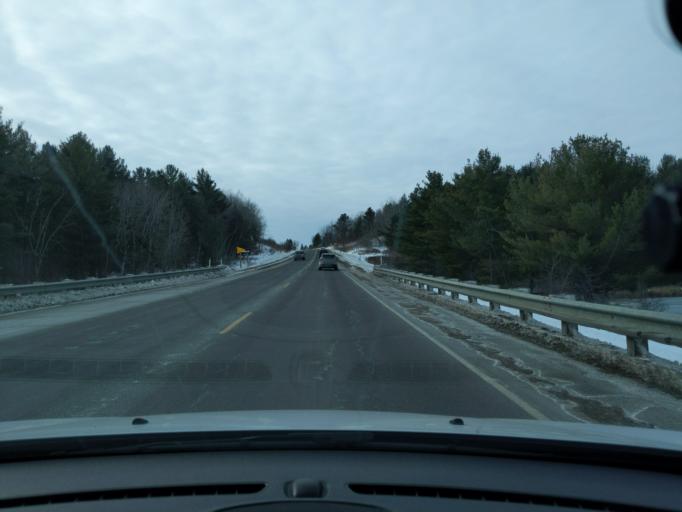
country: US
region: Wisconsin
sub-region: Polk County
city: Clear Lake
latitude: 45.2543
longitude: -92.2768
